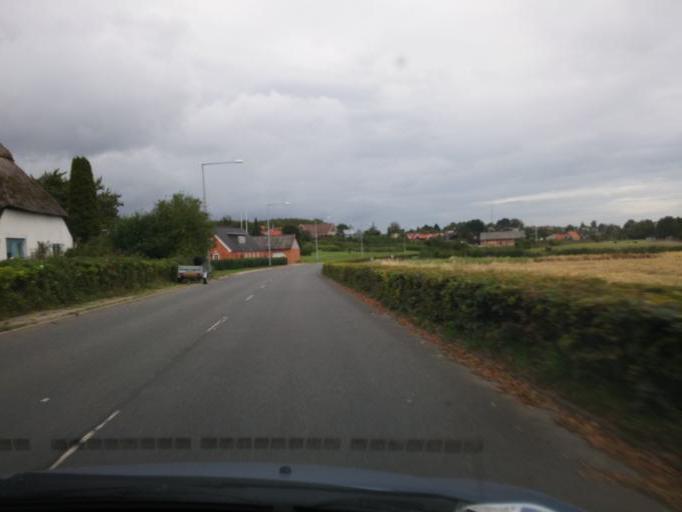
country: DK
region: South Denmark
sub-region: Kerteminde Kommune
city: Munkebo
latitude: 55.4439
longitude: 10.5408
